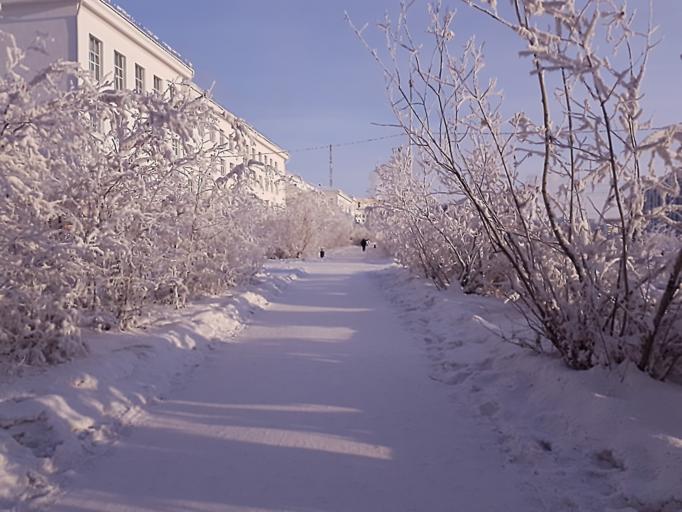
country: RU
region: Sakha
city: Yakutsk
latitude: 62.0187
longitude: 129.7077
